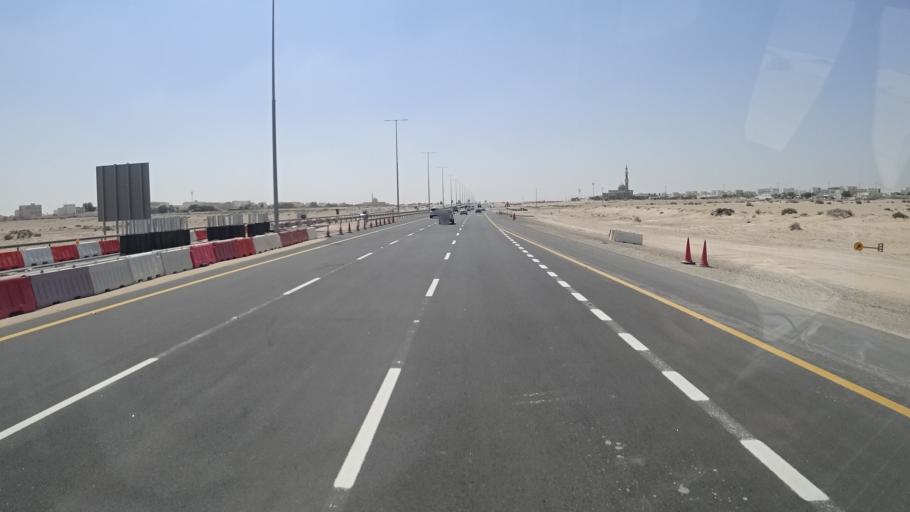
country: AE
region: Abu Dhabi
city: Abu Dhabi
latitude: 24.3356
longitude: 54.6978
